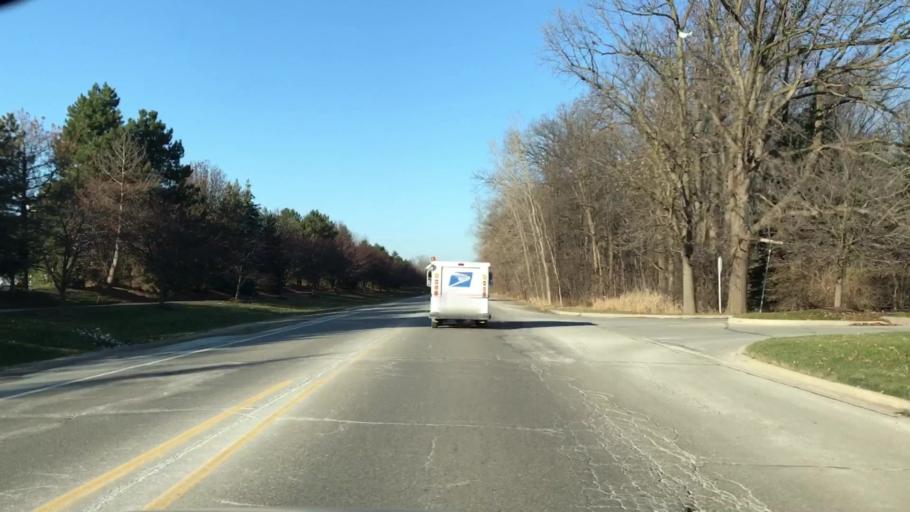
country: US
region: Michigan
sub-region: Oakland County
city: Novi
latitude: 42.4681
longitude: -83.5143
